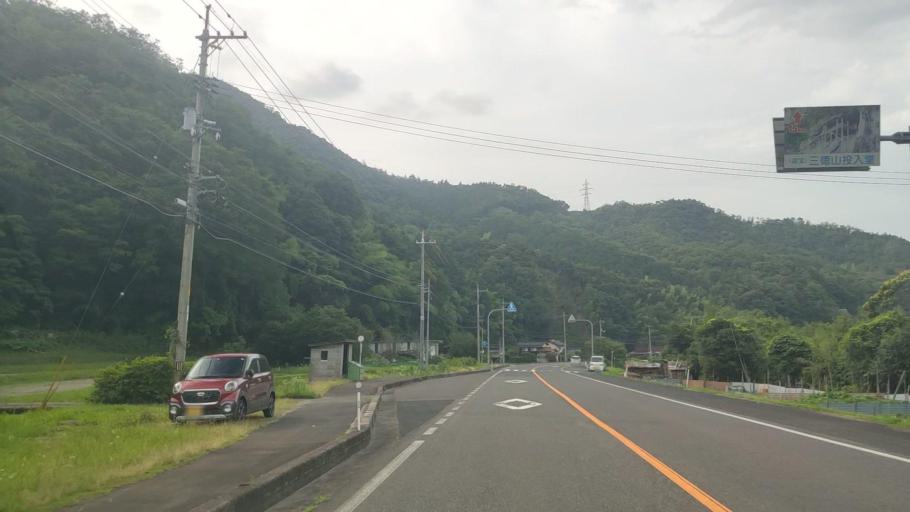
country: JP
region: Tottori
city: Kurayoshi
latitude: 35.3746
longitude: 133.8495
